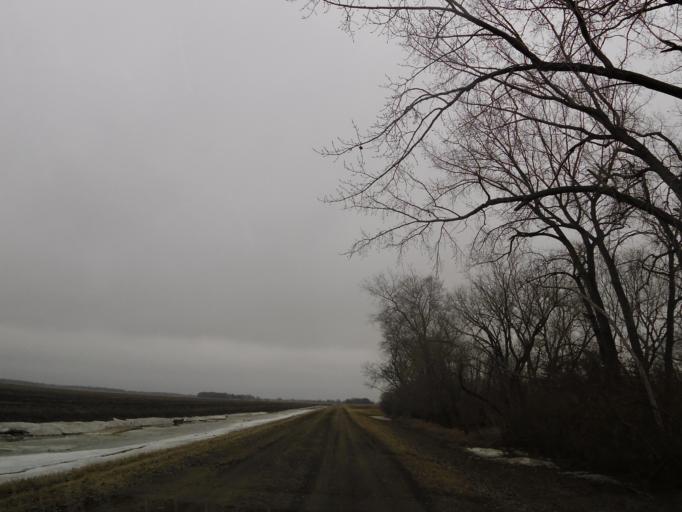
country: US
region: North Dakota
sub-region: Walsh County
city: Grafton
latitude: 48.3686
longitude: -97.1762
